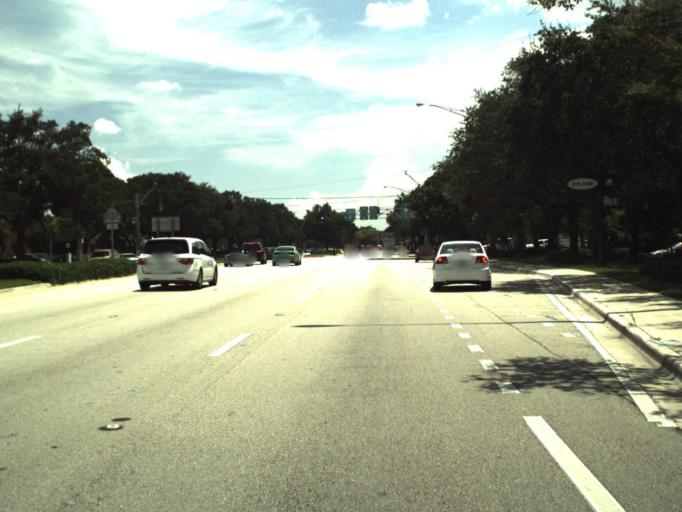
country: US
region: Florida
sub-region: Broward County
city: Tamarac
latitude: 26.2436
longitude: -80.2537
